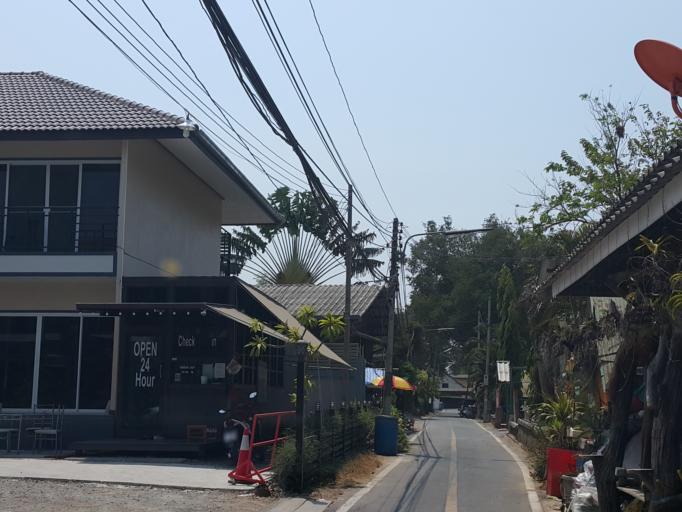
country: TH
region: Kanchanaburi
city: Kanchanaburi
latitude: 14.0304
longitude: 99.5221
